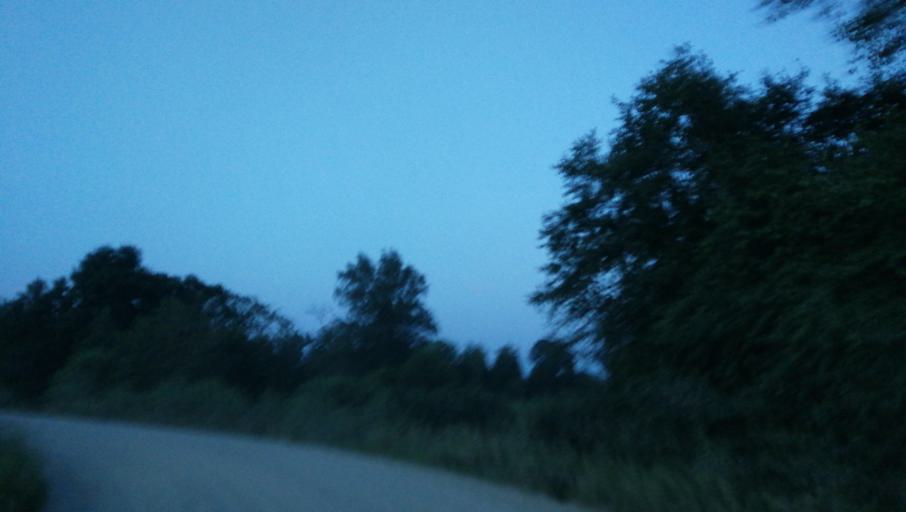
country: LV
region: Amatas Novads
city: Drabesi
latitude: 57.2445
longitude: 25.2017
